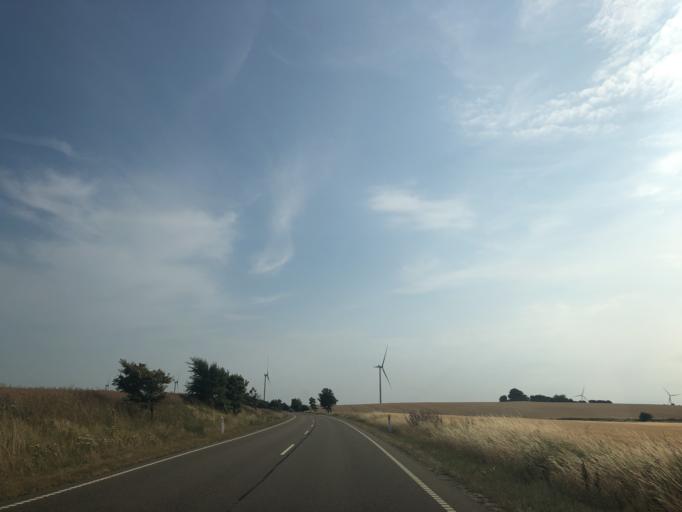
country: DK
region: North Denmark
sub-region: Morso Kommune
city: Nykobing Mors
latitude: 56.7779
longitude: 9.0361
